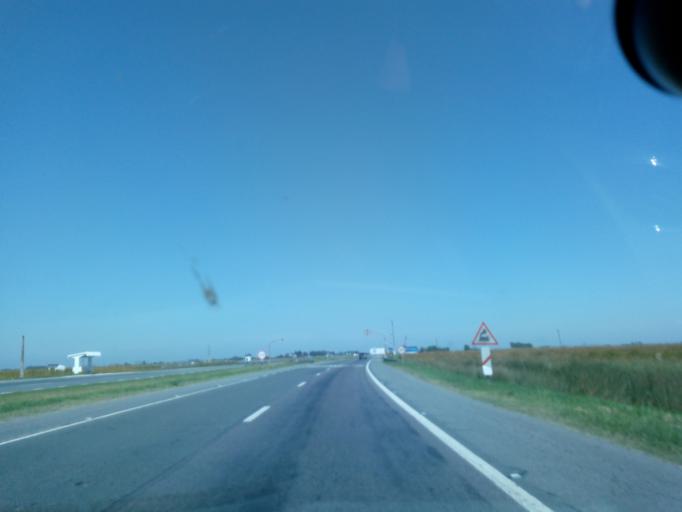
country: AR
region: Buenos Aires
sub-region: Partido de General Guido
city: General Guido
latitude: -36.6637
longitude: -57.7885
